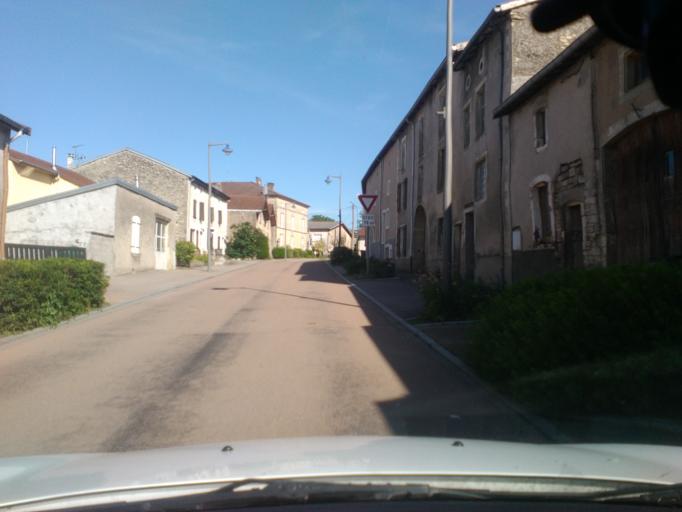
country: FR
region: Lorraine
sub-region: Departement des Vosges
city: Mirecourt
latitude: 48.2223
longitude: 6.2218
